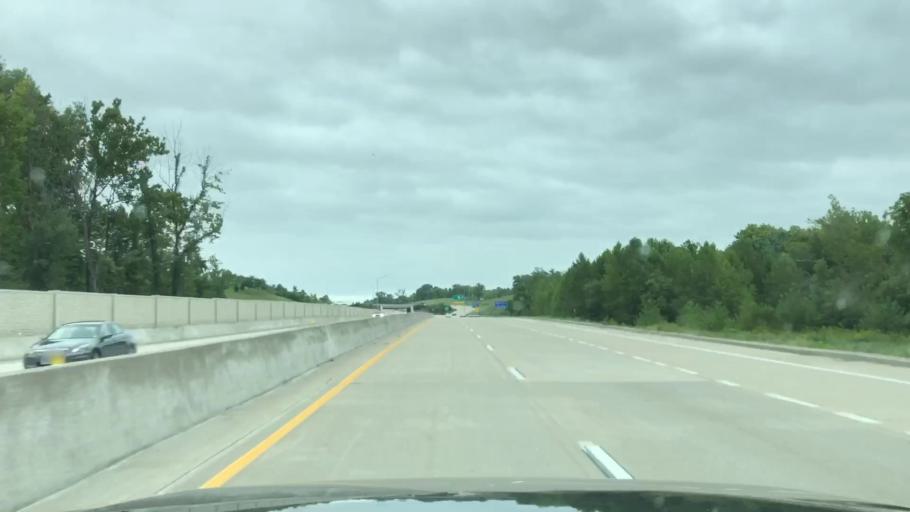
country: US
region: Missouri
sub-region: Saint Louis County
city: Town and Country
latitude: 38.6749
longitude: -90.4936
